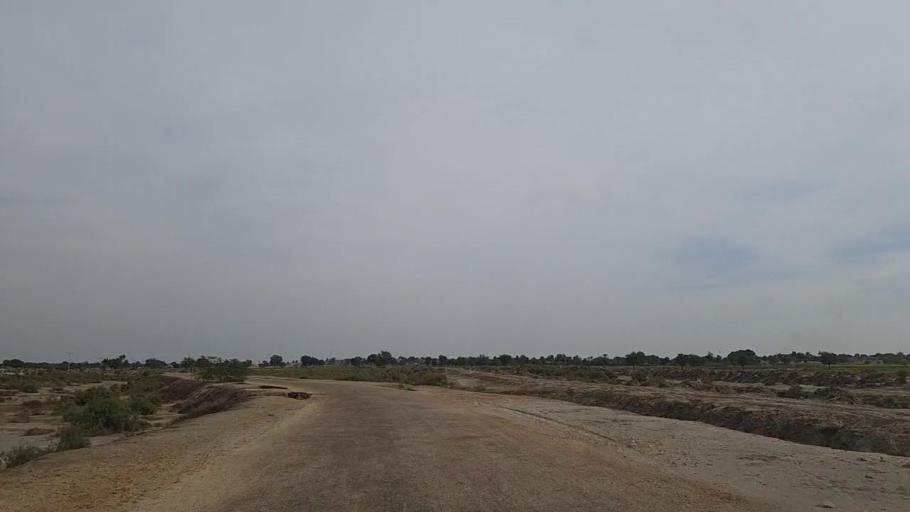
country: PK
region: Sindh
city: Jam Sahib
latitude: 26.3997
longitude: 68.5105
